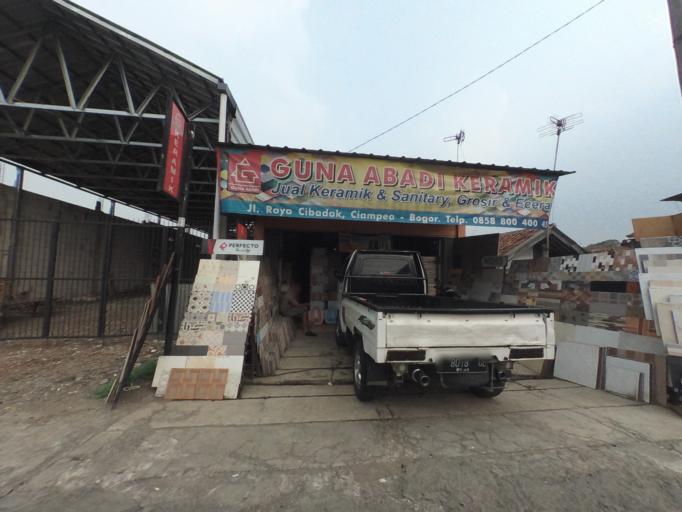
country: ID
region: West Java
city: Ciampea
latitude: -6.5601
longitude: 106.6858
